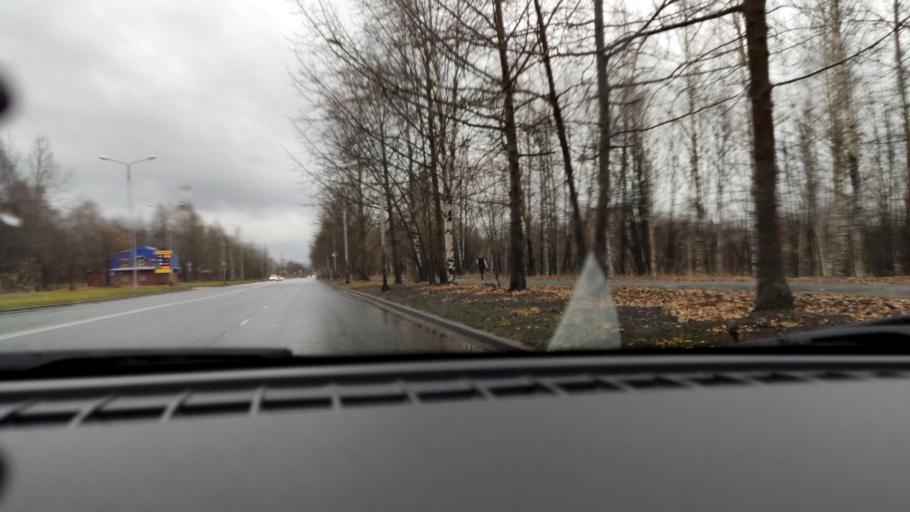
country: RU
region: Perm
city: Perm
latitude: 58.1046
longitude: 56.3931
